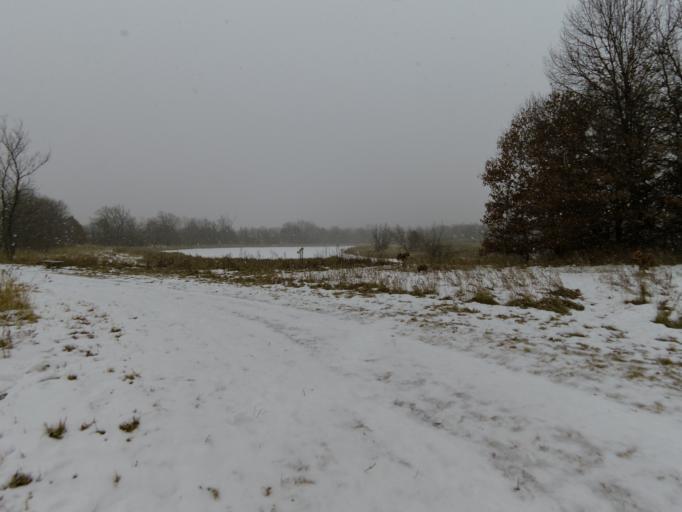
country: US
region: Minnesota
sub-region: Washington County
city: Lake Elmo
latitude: 44.9804
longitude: -92.9104
